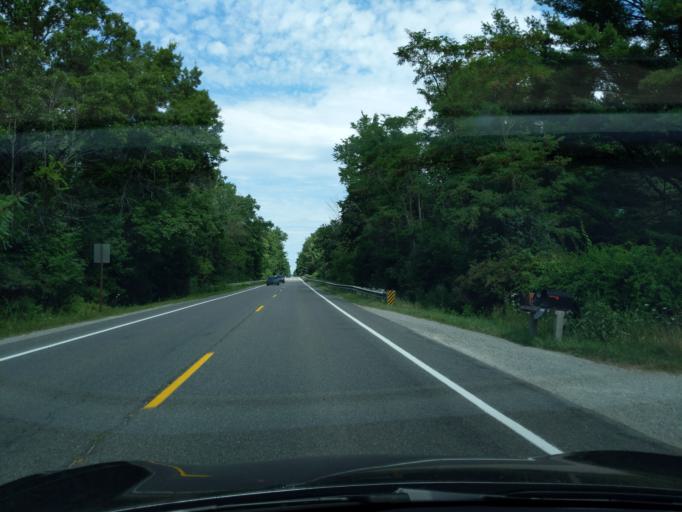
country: US
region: Michigan
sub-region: Midland County
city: Midland
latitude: 43.5931
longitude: -84.3694
